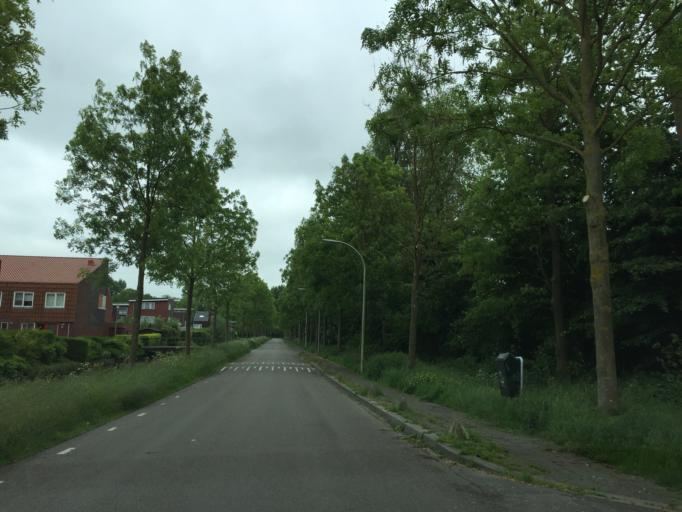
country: NL
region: South Holland
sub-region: Gemeente Den Haag
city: Ypenburg
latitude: 52.0298
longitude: 4.3766
